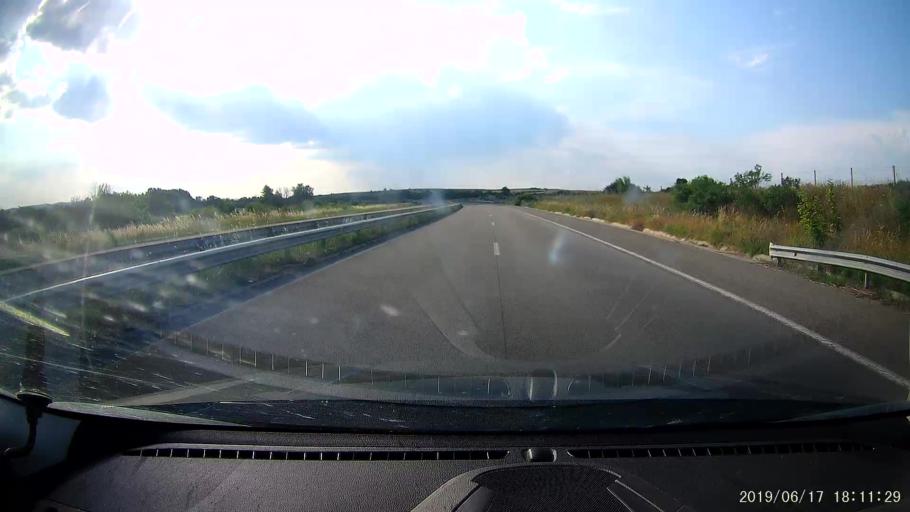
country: BG
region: Khaskovo
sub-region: Obshtina Lyubimets
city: Lyubimets
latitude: 41.8850
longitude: 26.0504
